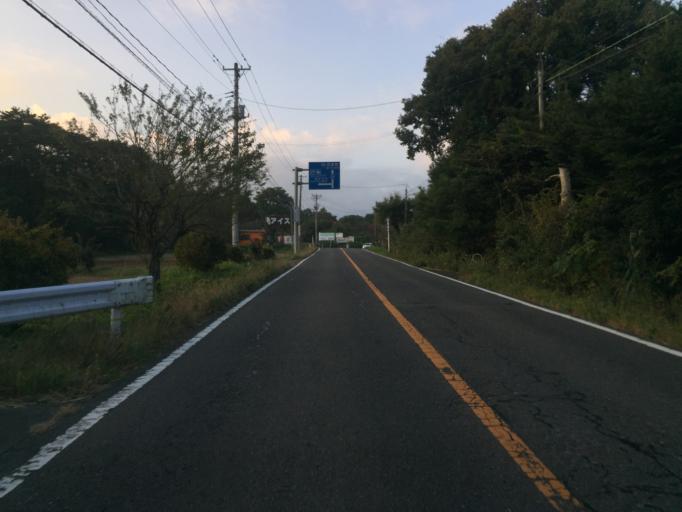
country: JP
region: Fukushima
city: Motomiya
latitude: 37.5707
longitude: 140.3513
